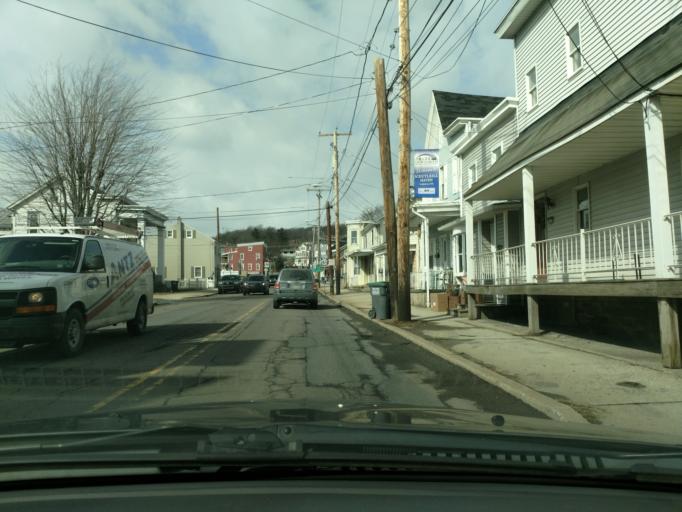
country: US
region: Pennsylvania
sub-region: Schuylkill County
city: Schuylkill Haven
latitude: 40.6360
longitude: -76.1755
